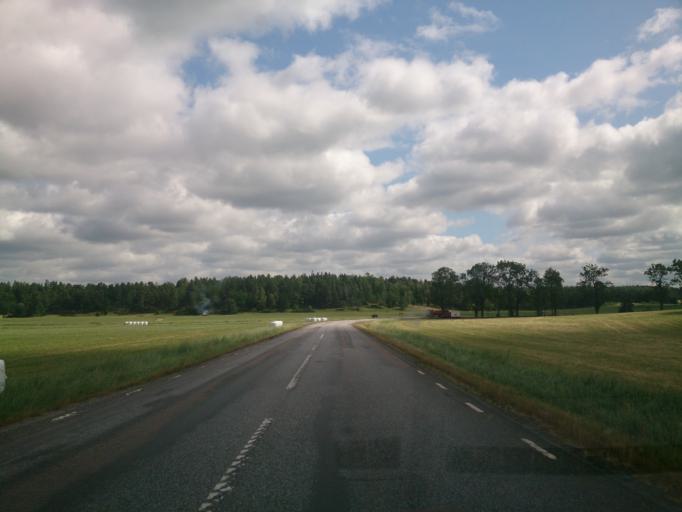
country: SE
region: OEstergoetland
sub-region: Norrkopings Kommun
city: Kimstad
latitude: 58.4821
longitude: 15.9501
